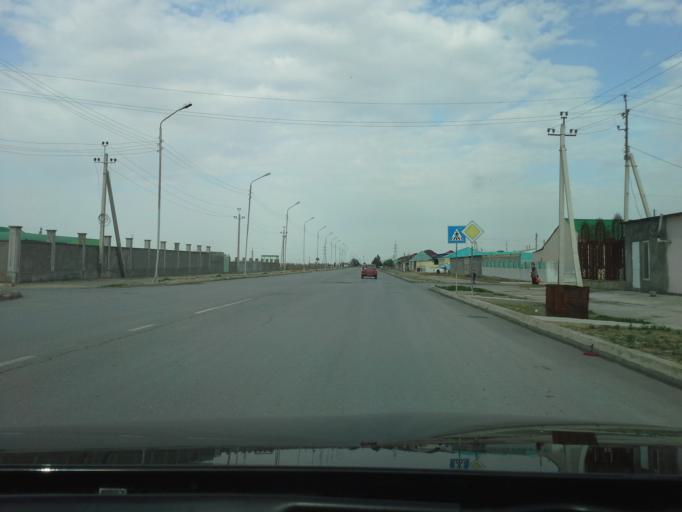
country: TM
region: Ahal
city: Ashgabat
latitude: 37.9913
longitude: 58.2901
